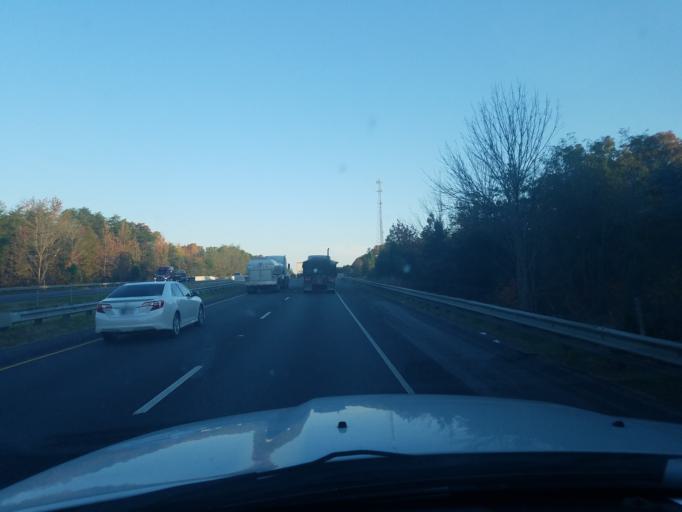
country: US
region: Indiana
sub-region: Clark County
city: Henryville
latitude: 38.5687
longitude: -85.7787
